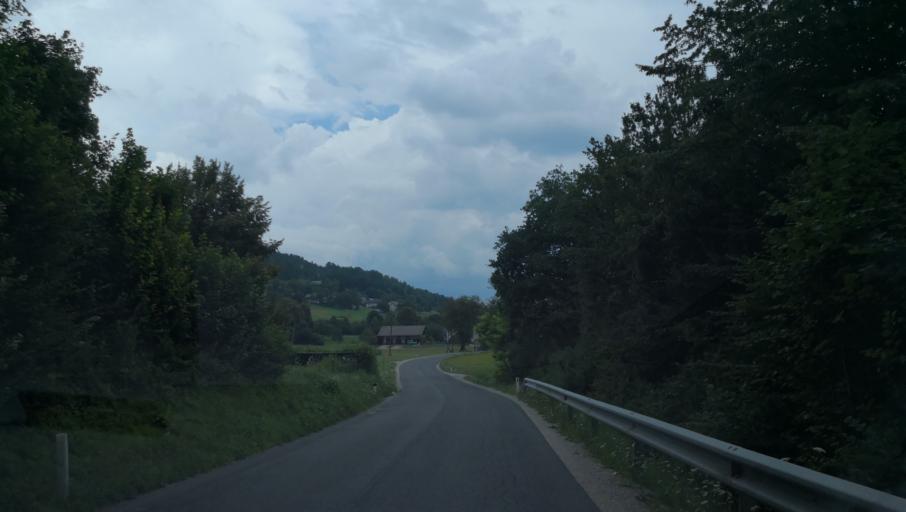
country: SI
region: Zuzemberk
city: Zuzemberk
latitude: 45.8580
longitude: 14.8550
